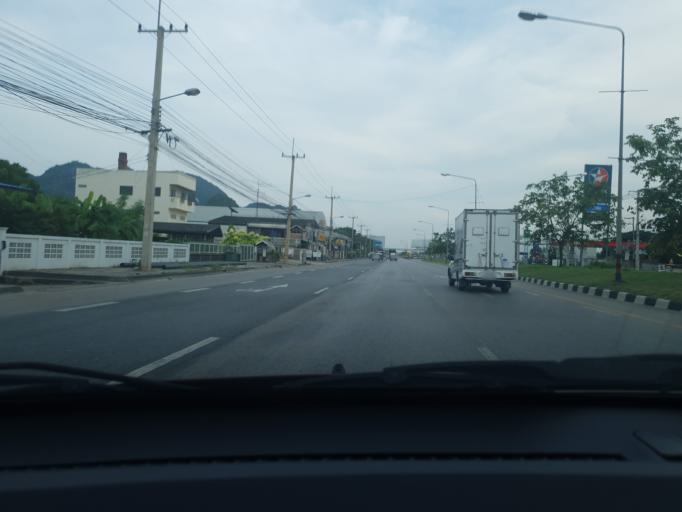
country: TH
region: Phetchaburi
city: Cha-am
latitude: 12.8439
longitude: 99.9291
